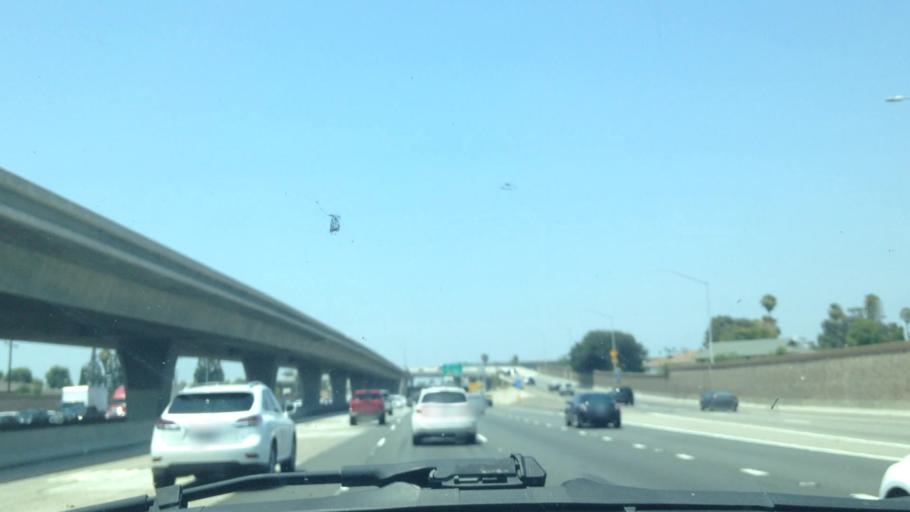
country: US
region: California
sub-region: Orange County
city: Tustin
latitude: 33.7358
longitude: -117.8337
